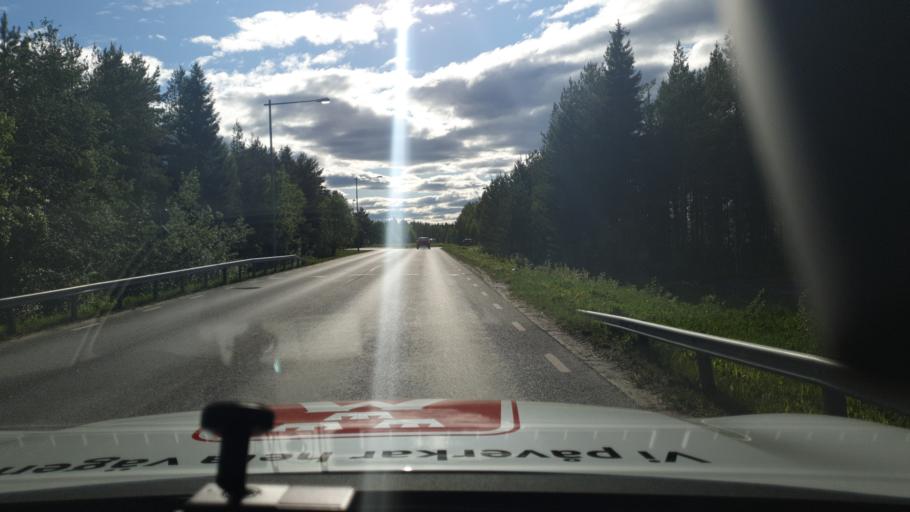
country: SE
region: Vaesterbotten
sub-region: Umea Kommun
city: Ersmark
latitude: 63.8025
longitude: 20.3520
